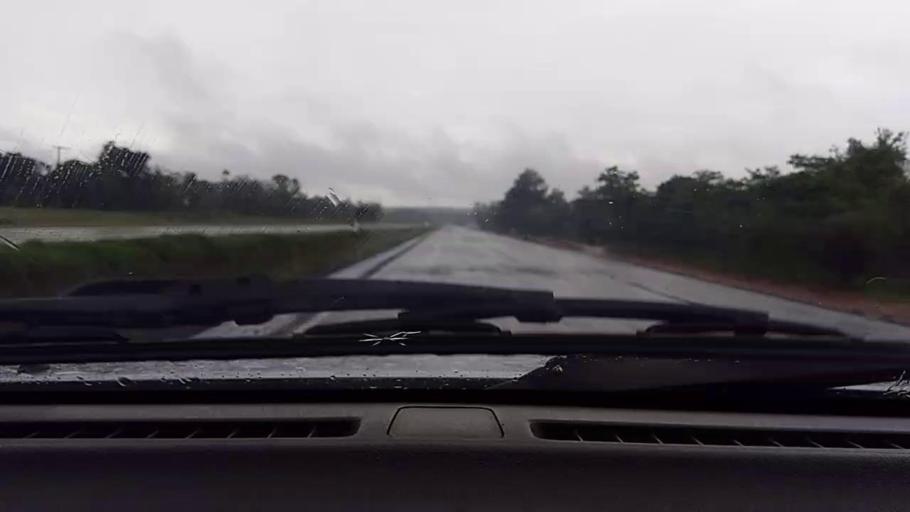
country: PY
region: Caaguazu
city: Repatriacion
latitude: -25.4629
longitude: -55.9280
